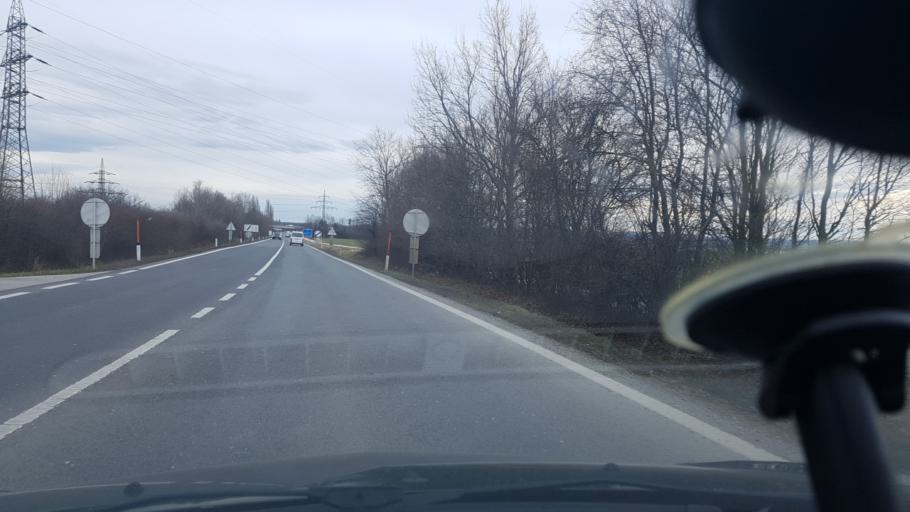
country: AT
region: Burgenland
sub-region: Eisenstadt Stadt
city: Eisenstadt
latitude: 47.8440
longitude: 16.5448
